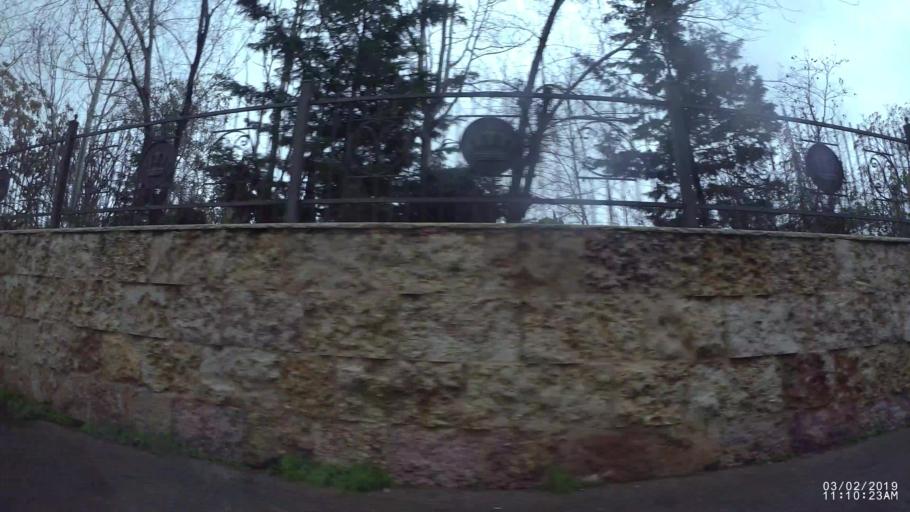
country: JO
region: Amman
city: Amman
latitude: 31.9511
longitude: 35.9215
